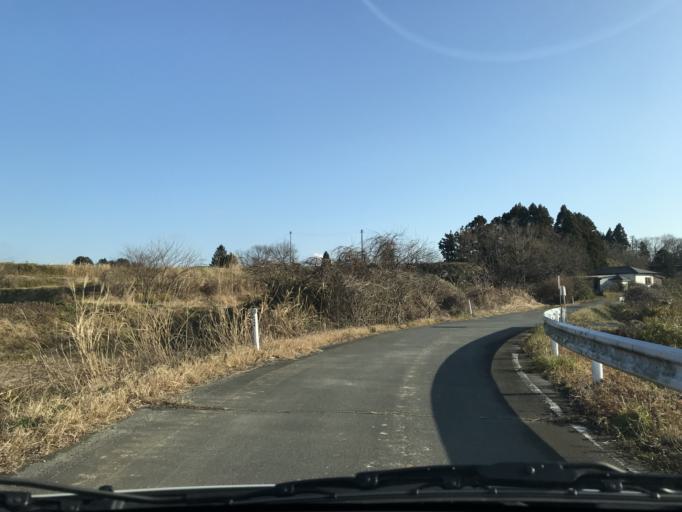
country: JP
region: Miyagi
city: Wakuya
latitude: 38.6883
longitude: 141.1291
